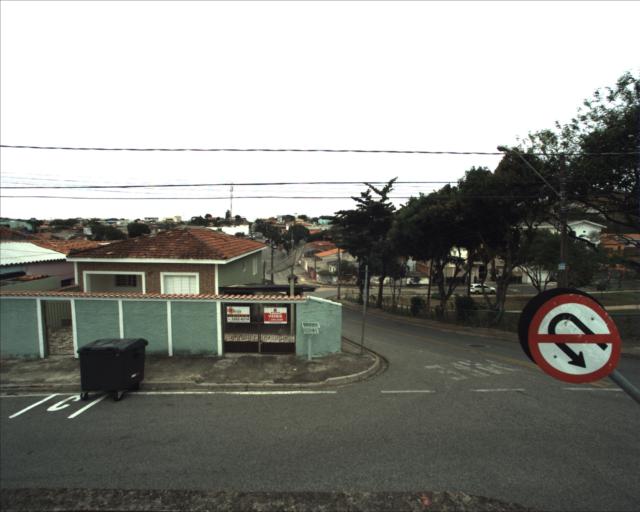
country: BR
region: Sao Paulo
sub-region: Votorantim
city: Votorantim
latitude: -23.5208
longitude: -47.4392
